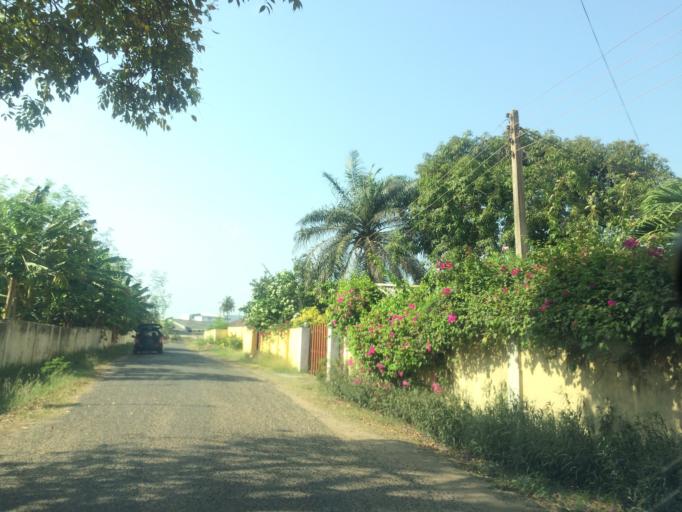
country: GH
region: Greater Accra
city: Accra
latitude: 5.5573
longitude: -0.1699
